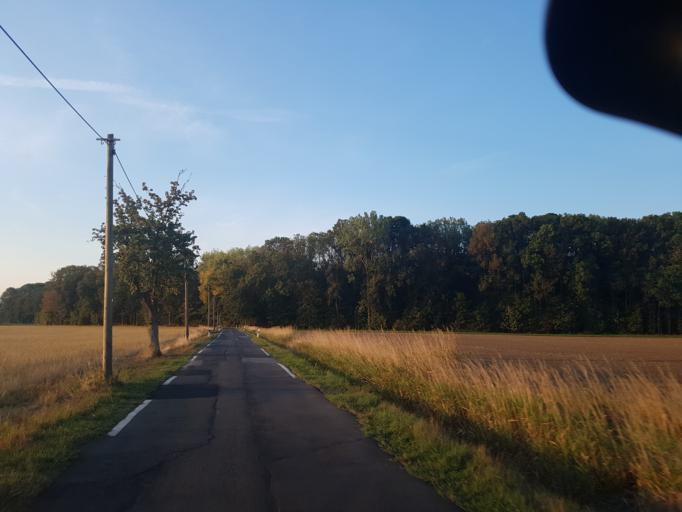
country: DE
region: Saxony
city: Stauchitz
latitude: 51.2669
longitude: 13.1861
